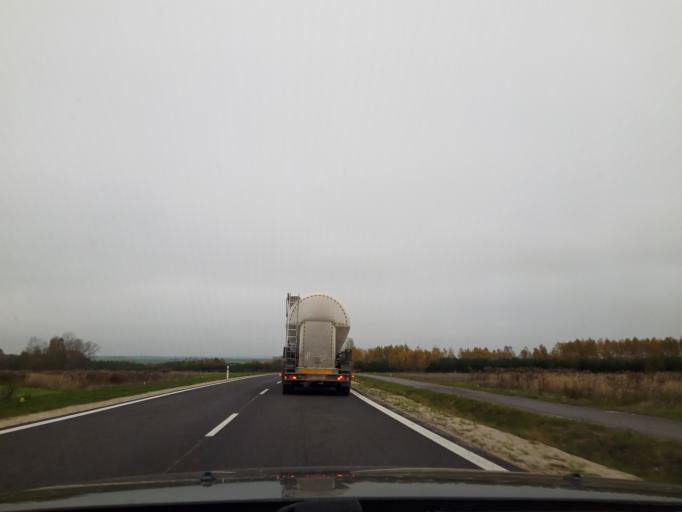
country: PL
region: Swietokrzyskie
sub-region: Powiat jedrzejowski
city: Jedrzejow
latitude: 50.6218
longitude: 20.3177
